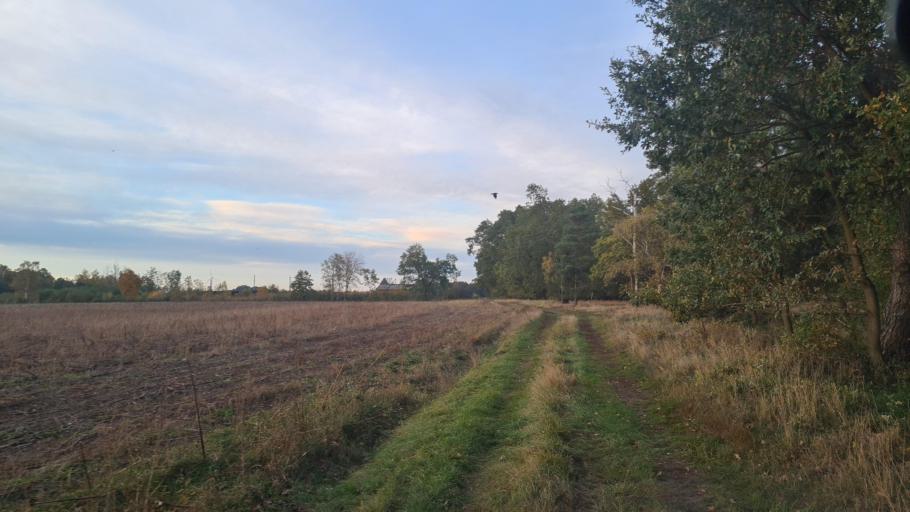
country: DE
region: Brandenburg
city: Bad Liebenwerda
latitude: 51.5361
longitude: 13.3389
